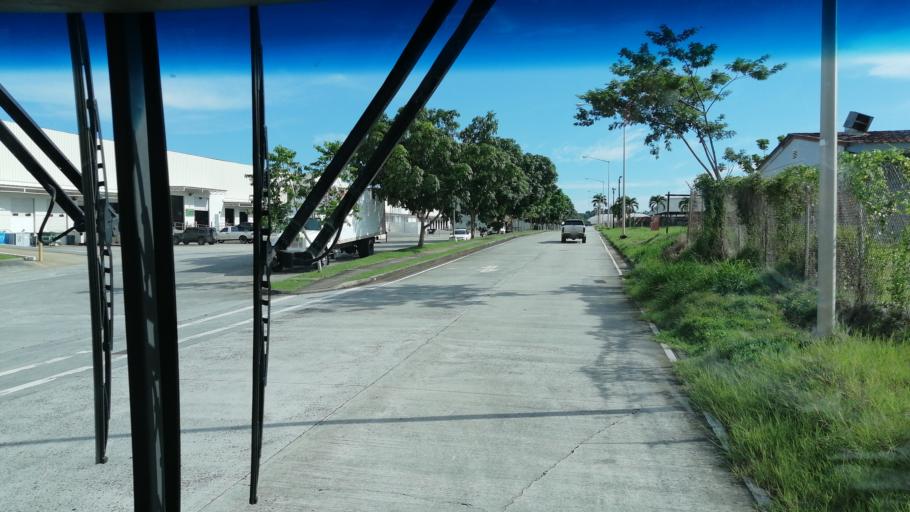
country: PA
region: Panama
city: Veracruz
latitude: 8.9226
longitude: -79.5944
